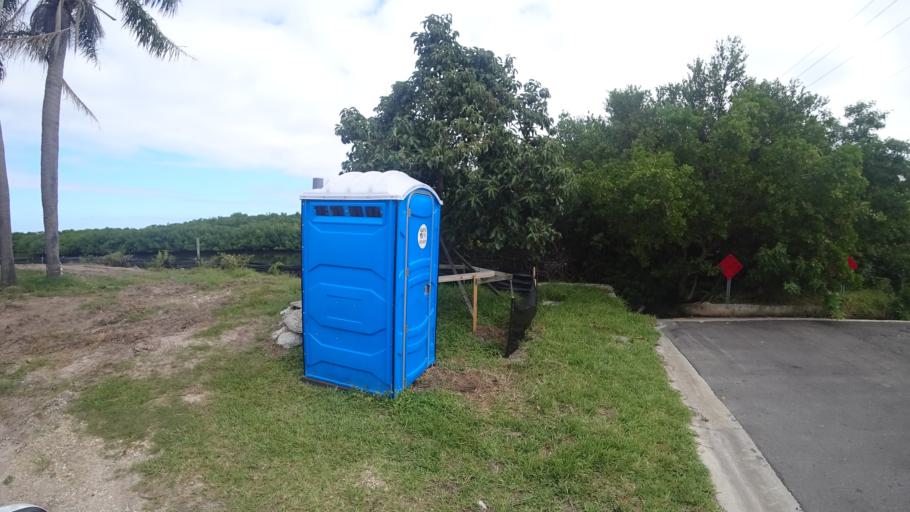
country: US
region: Florida
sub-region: Manatee County
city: Longboat Key
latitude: 27.4210
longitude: -82.6591
